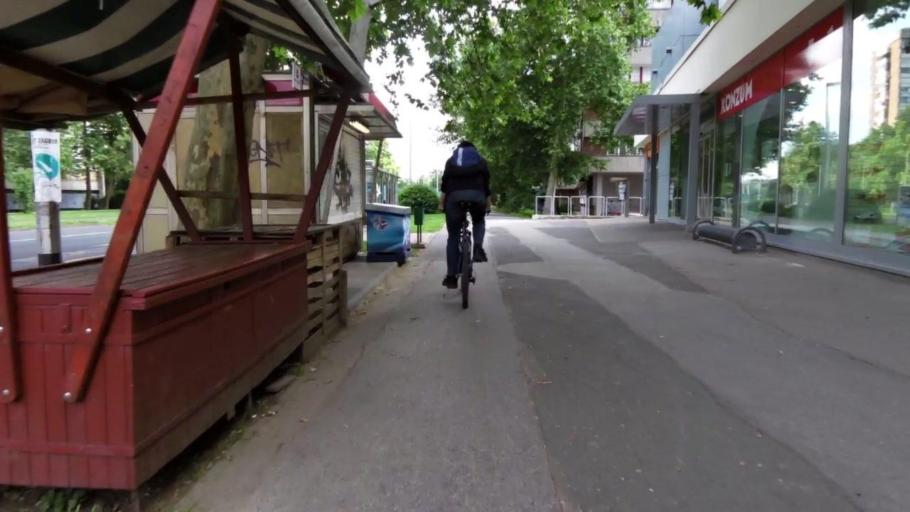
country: HR
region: Grad Zagreb
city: Novi Zagreb
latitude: 45.7911
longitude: 15.9446
